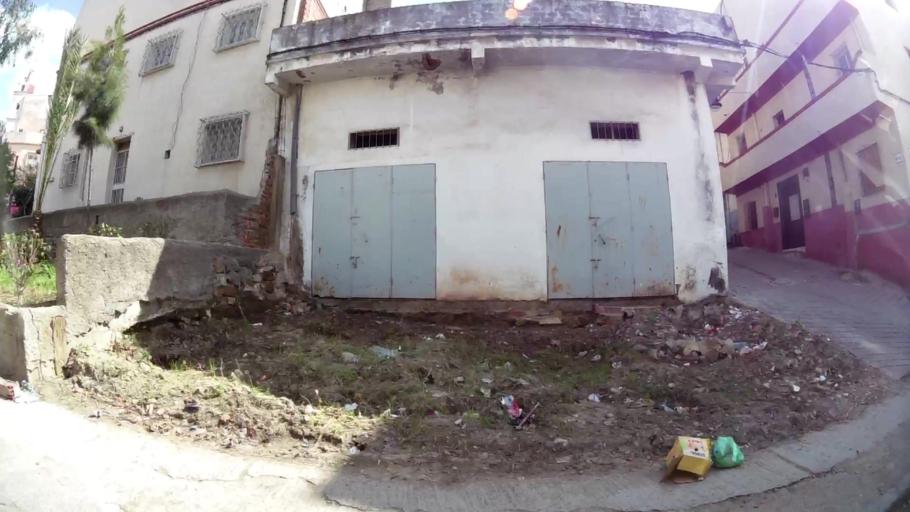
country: MA
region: Tanger-Tetouan
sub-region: Tanger-Assilah
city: Tangier
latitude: 35.7706
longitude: -5.7690
